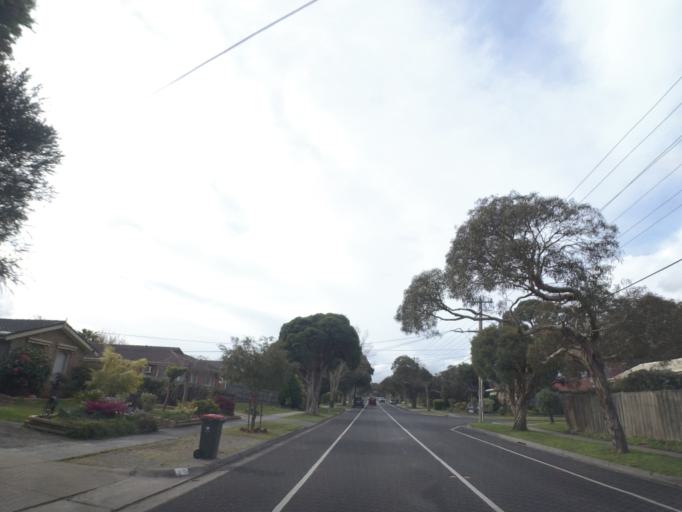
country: AU
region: Victoria
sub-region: Whitehorse
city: Vermont South
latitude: -37.8663
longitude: 145.1811
